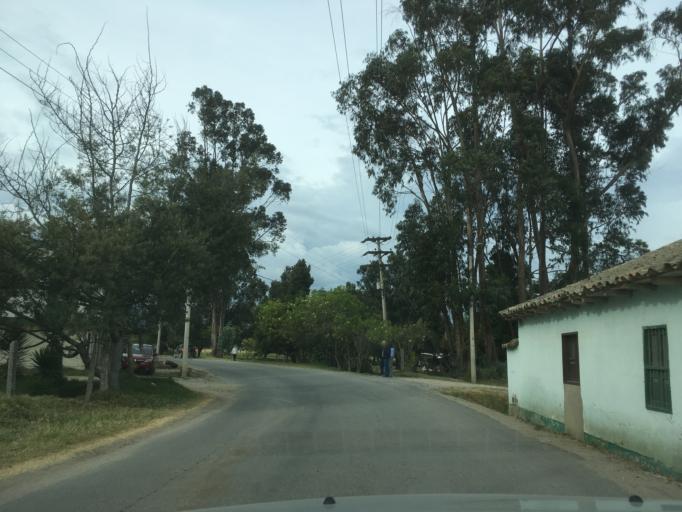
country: CO
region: Boyaca
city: Firavitoba
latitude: 5.6522
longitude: -72.9889
